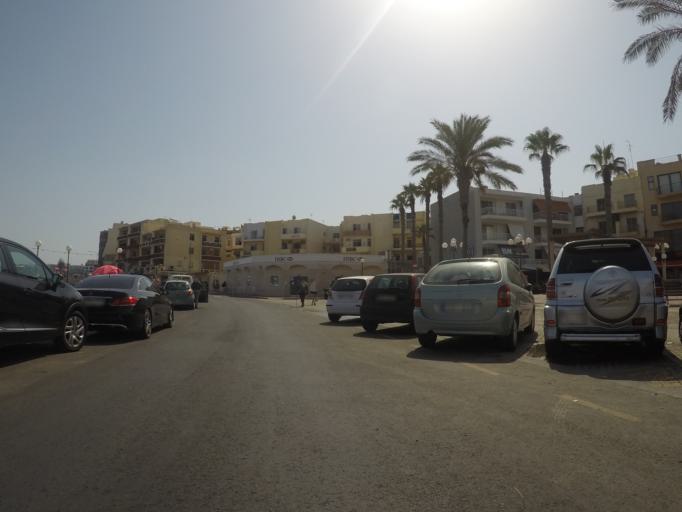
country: MT
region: Saint Paul's Bay
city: San Pawl il-Bahar
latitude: 35.9519
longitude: 14.4138
